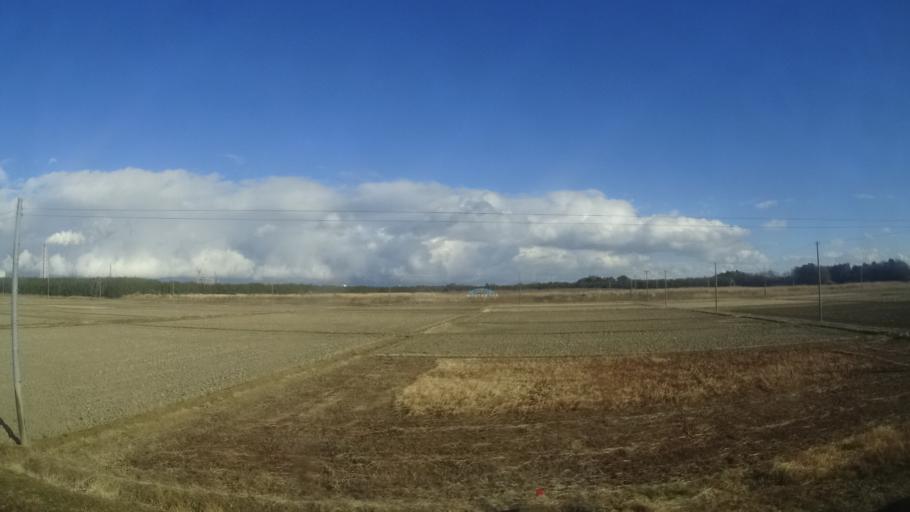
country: JP
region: Miyagi
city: Marumori
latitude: 37.8254
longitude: 140.9255
